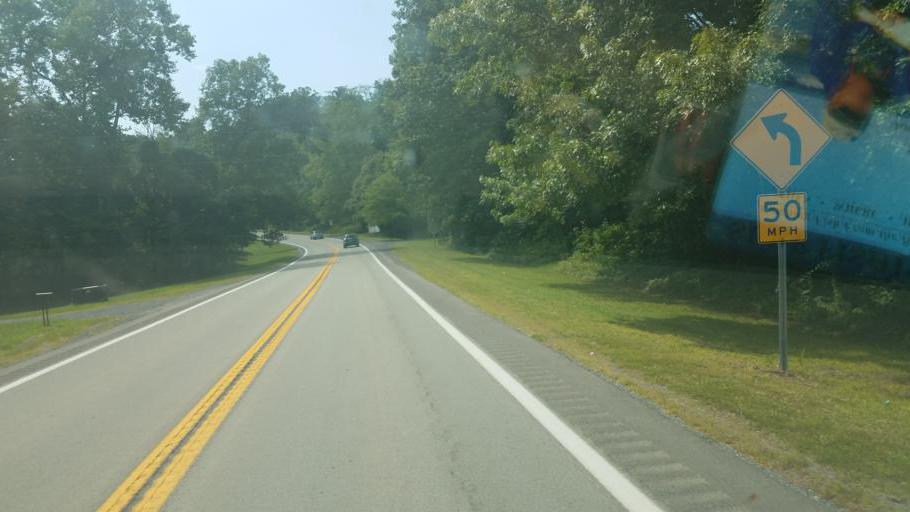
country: US
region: Virginia
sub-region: Frederick County
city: Shawnee Land
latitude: 39.3581
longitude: -78.3632
